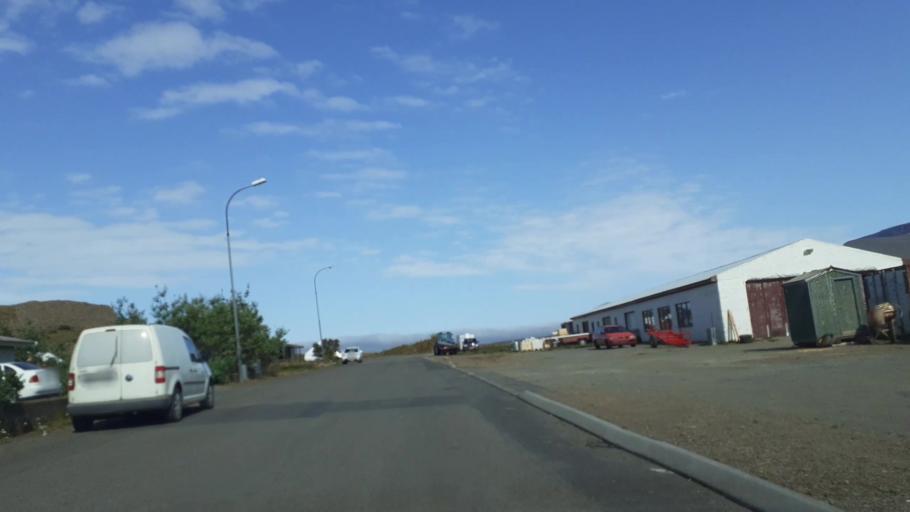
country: IS
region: Northwest
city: Saudarkrokur
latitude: 65.8279
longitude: -20.3163
